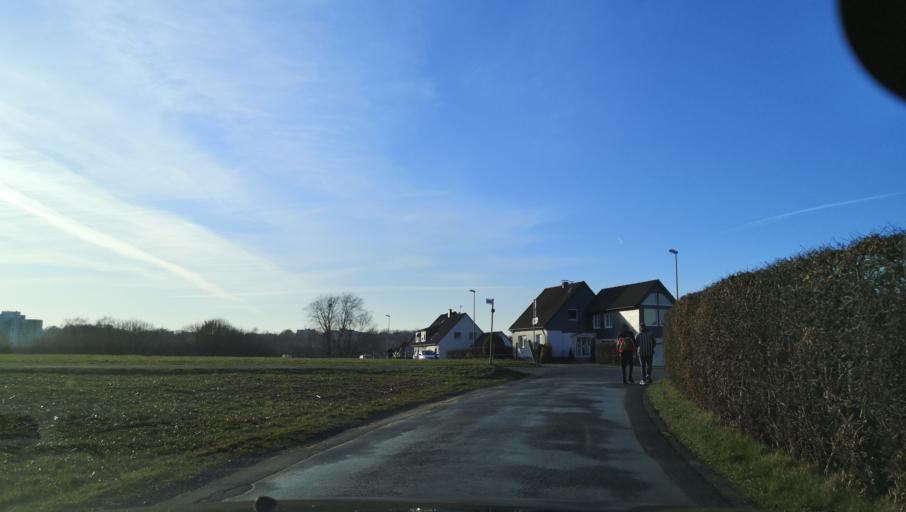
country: DE
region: North Rhine-Westphalia
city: Radevormwald
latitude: 51.1990
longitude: 7.2870
